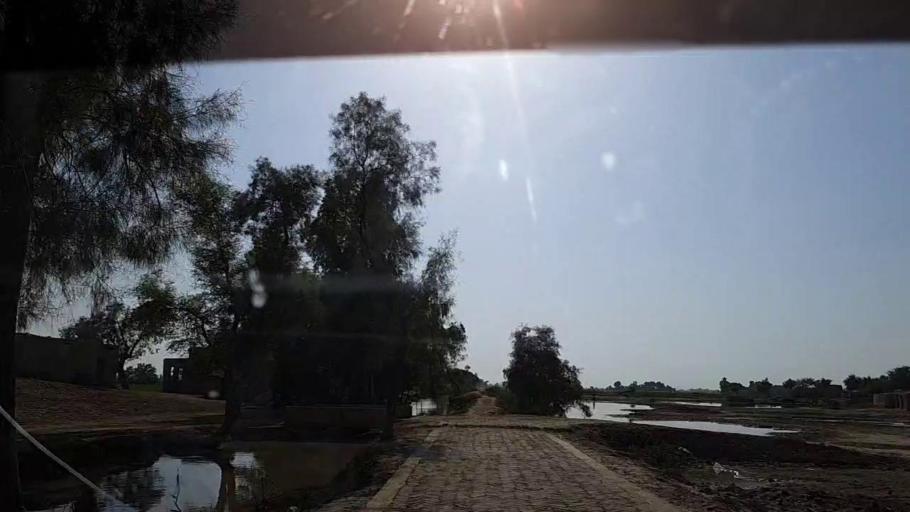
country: PK
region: Sindh
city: Tangwani
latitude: 28.2138
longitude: 68.9623
